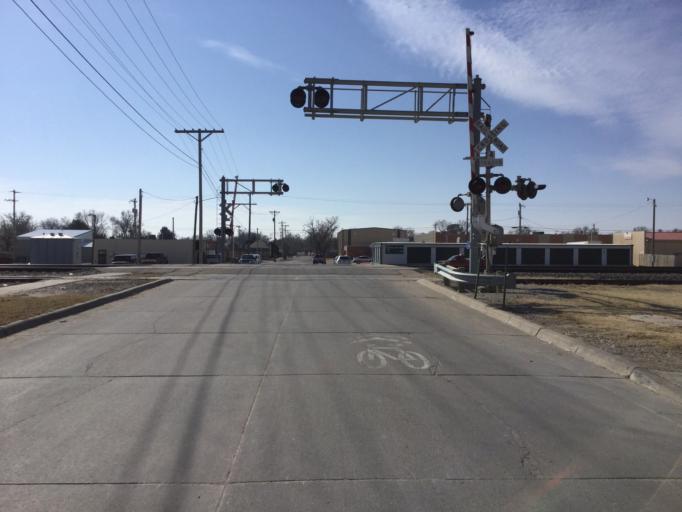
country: US
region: Kansas
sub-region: Ellis County
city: Hays
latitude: 38.8697
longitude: -99.3260
